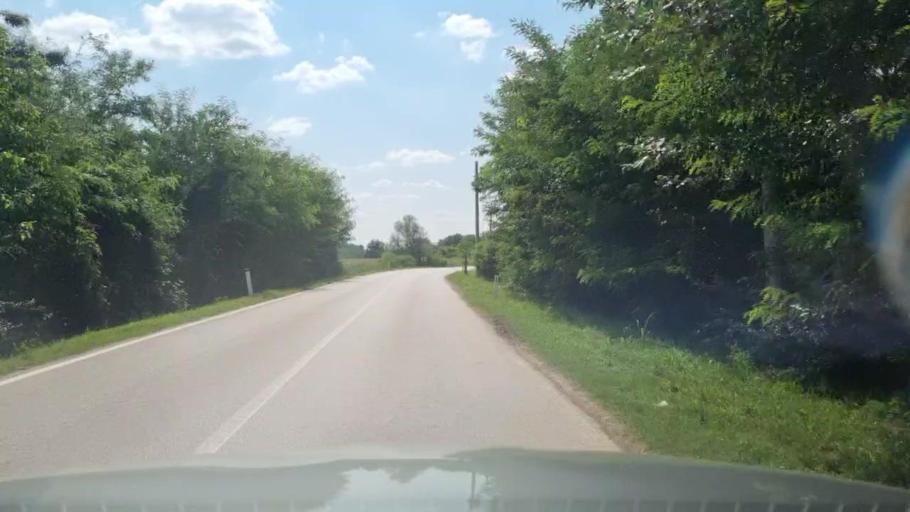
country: BA
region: Federation of Bosnia and Herzegovina
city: Donja Dubica
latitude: 45.0650
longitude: 18.4234
